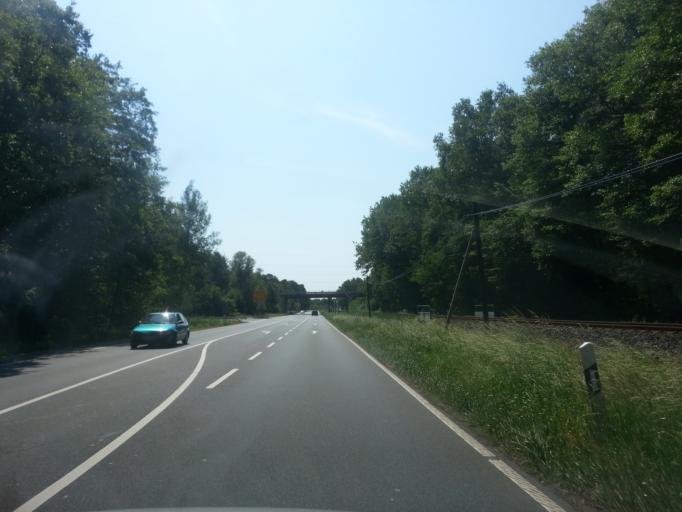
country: DE
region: Hesse
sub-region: Regierungsbezirk Darmstadt
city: Eppertshausen
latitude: 49.9578
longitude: 8.8367
